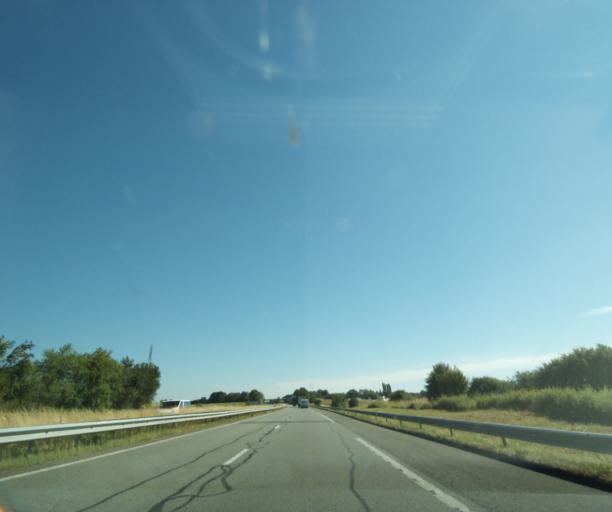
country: FR
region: Champagne-Ardenne
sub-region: Departement de la Haute-Marne
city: Avrecourt
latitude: 47.9883
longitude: 5.5097
